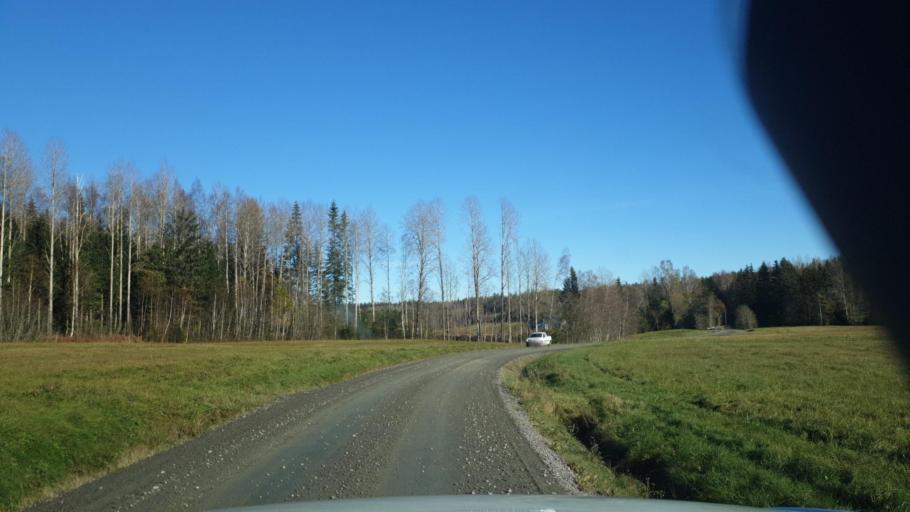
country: SE
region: Vaermland
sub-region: Karlstads Kommun
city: Edsvalla
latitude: 59.5014
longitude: 13.1904
